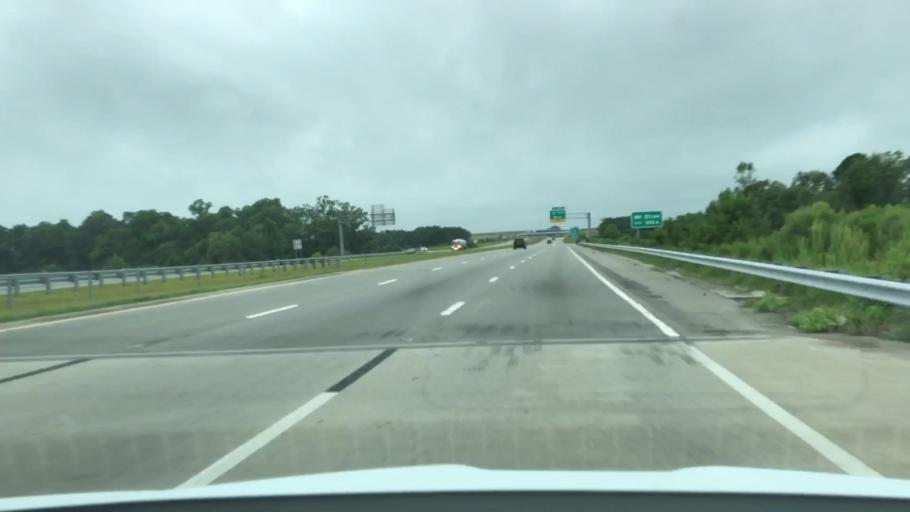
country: US
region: North Carolina
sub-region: Wayne County
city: Goldsboro
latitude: 35.4261
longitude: -77.9841
